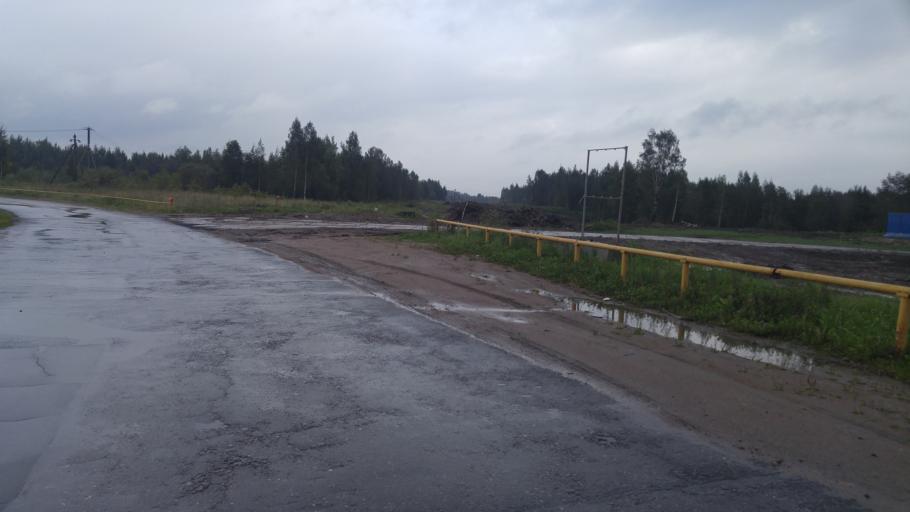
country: RU
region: St.-Petersburg
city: Ust'-Izhora
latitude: 59.7854
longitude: 30.5757
